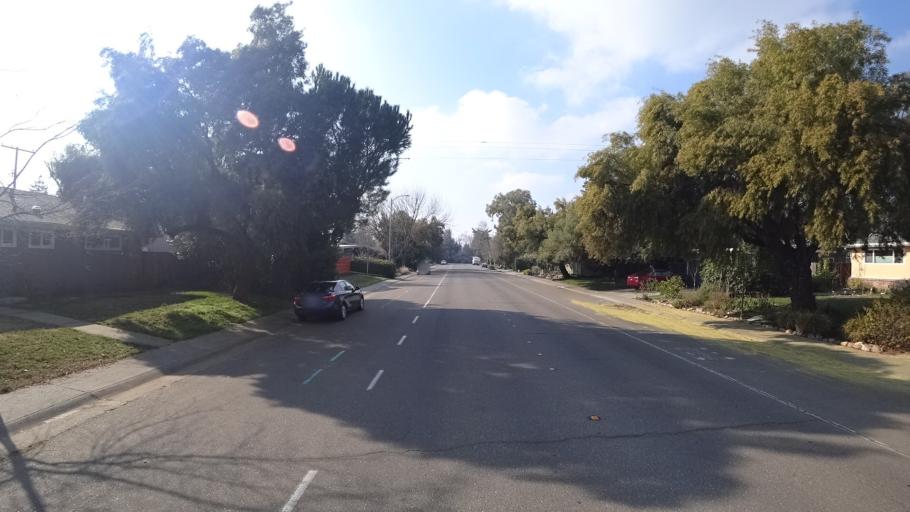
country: US
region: California
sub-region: Yolo County
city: Davis
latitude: 38.5562
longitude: -121.7627
